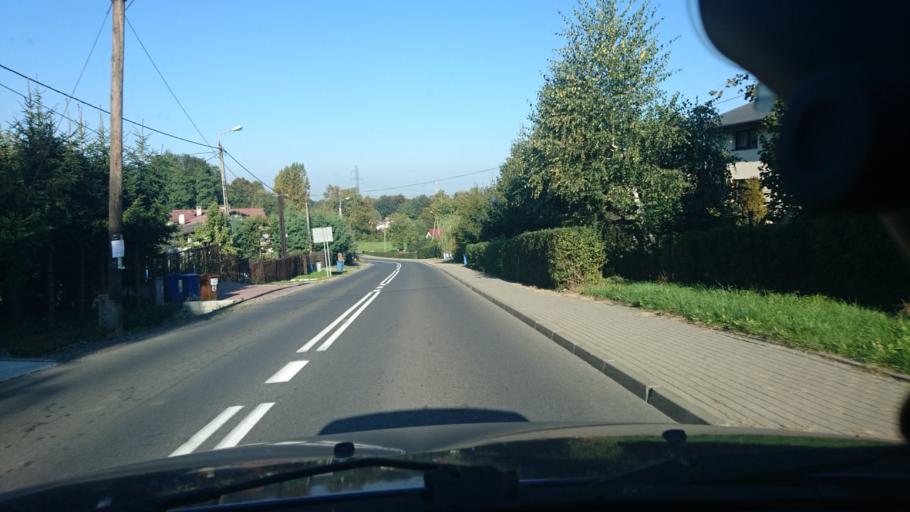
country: PL
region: Silesian Voivodeship
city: Janowice
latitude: 49.8502
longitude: 19.0832
